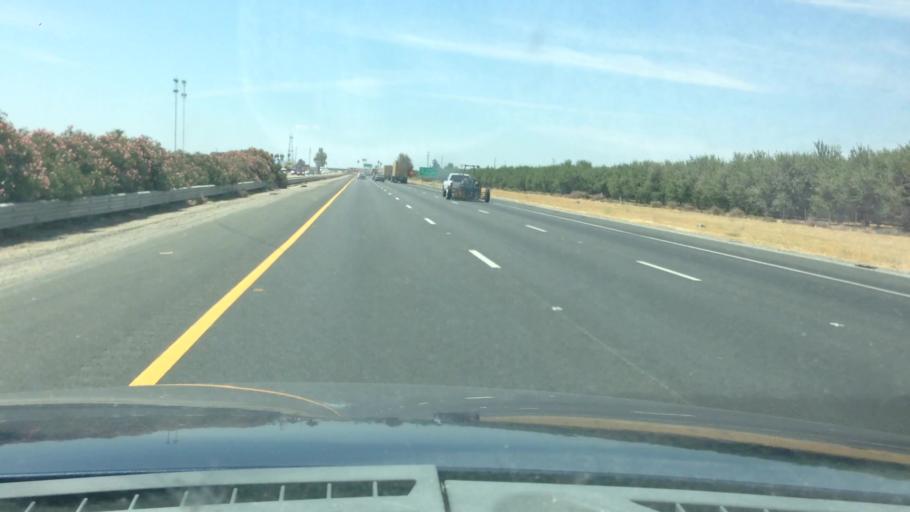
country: US
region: California
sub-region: Kern County
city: McFarland
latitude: 35.6126
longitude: -119.2120
